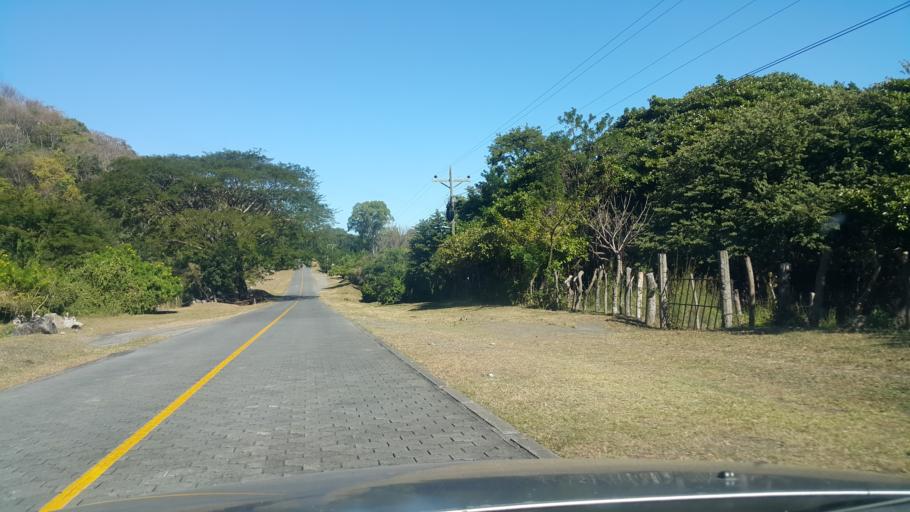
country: NI
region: Rivas
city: Altagracia
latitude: 11.4957
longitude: -85.6249
